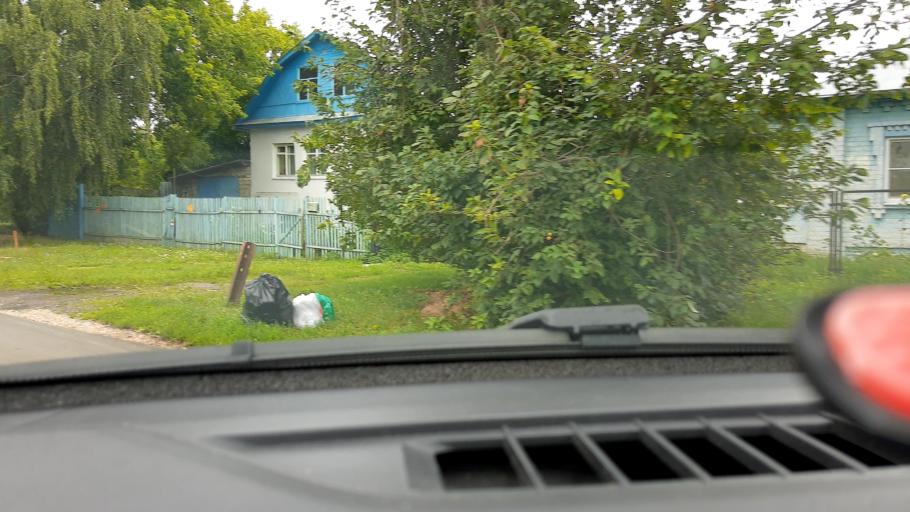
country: RU
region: Nizjnij Novgorod
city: Gorbatovka
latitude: 56.2634
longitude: 43.7542
